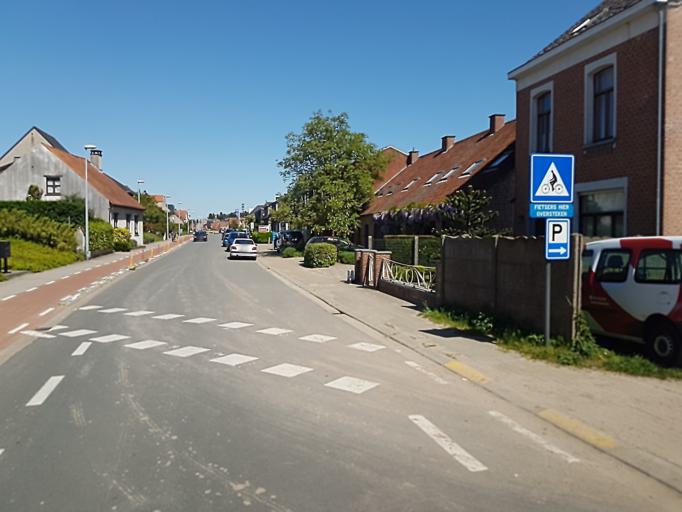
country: BE
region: Flanders
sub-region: Provincie Antwerpen
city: Kasterlee
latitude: 51.2418
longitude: 4.9710
